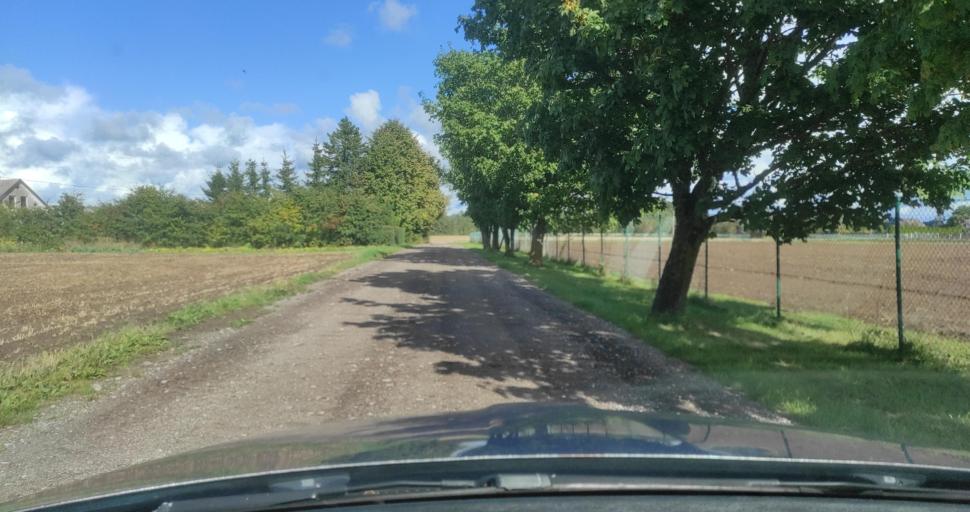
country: LV
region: Ventspils Rajons
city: Piltene
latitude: 57.2650
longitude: 21.6035
